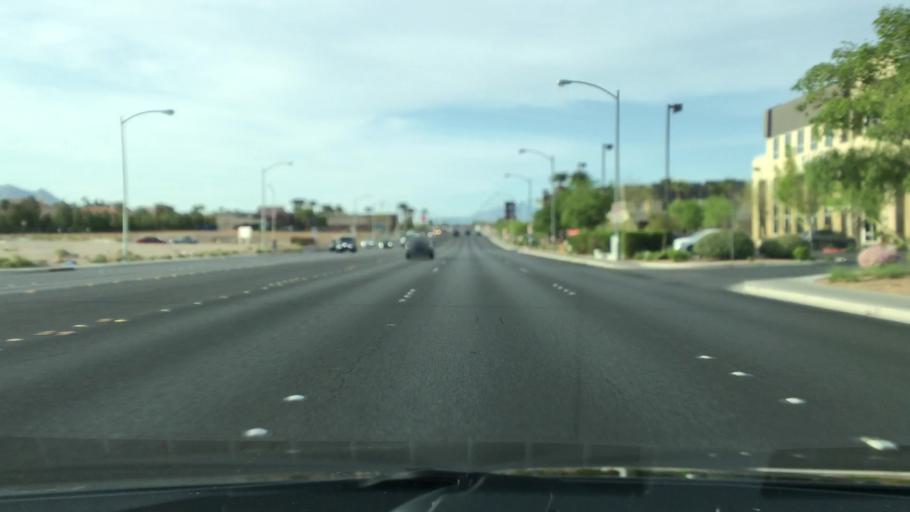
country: US
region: Nevada
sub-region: Clark County
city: Summerlin South
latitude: 36.1026
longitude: -115.2972
